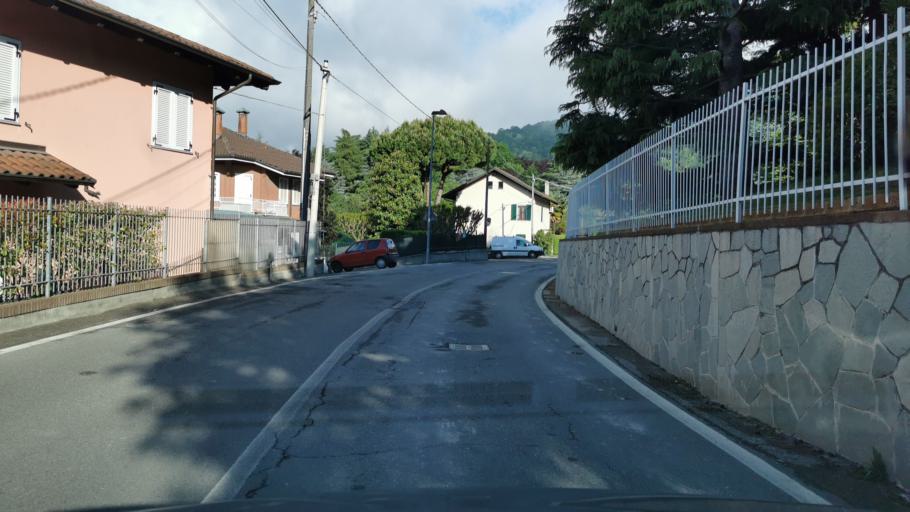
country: IT
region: Piedmont
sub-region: Provincia di Torino
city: Pino Torinese
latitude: 45.0344
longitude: 7.7734
